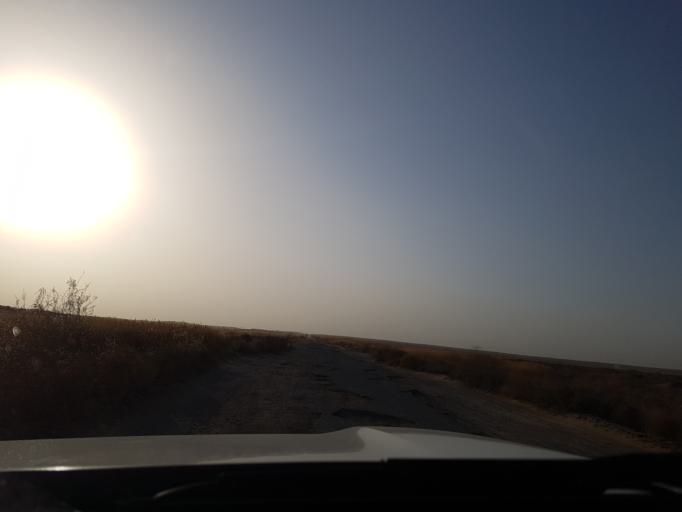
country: UZ
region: Xorazm
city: Hazorasp
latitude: 41.1649
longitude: 60.7613
